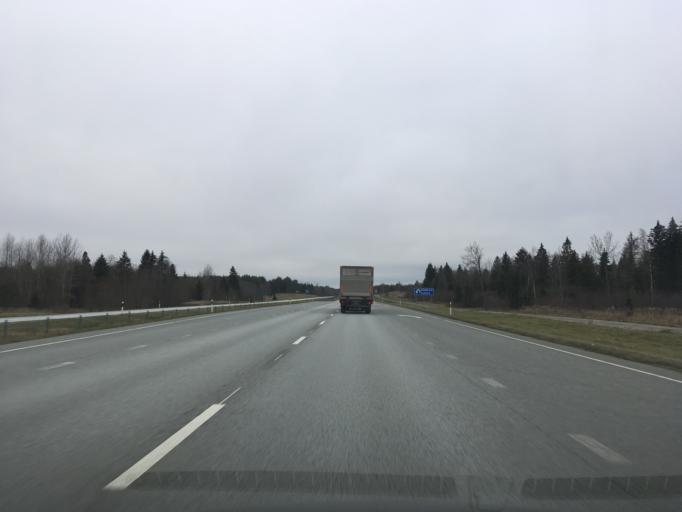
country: EE
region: Laeaene-Virumaa
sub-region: Kadrina vald
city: Kadrina
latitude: 59.4495
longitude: 26.0707
